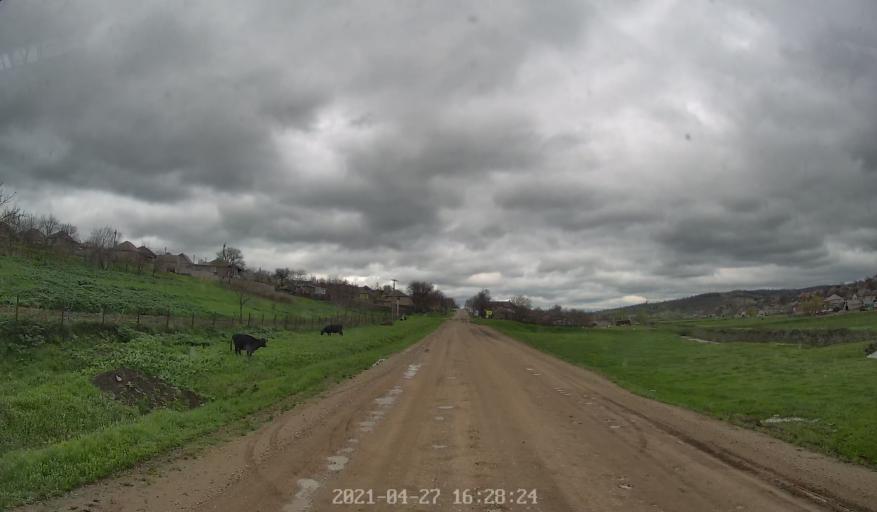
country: MD
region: Chisinau
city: Singera
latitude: 46.9719
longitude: 29.0418
